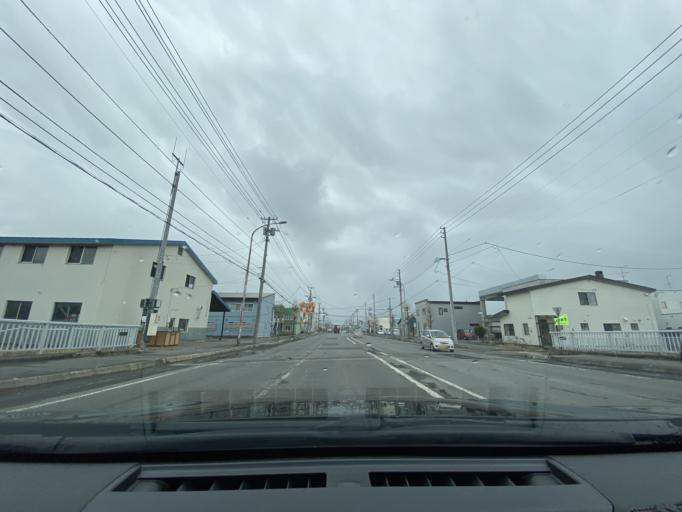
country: JP
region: Hokkaido
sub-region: Asahikawa-shi
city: Asahikawa
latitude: 43.8126
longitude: 142.3762
